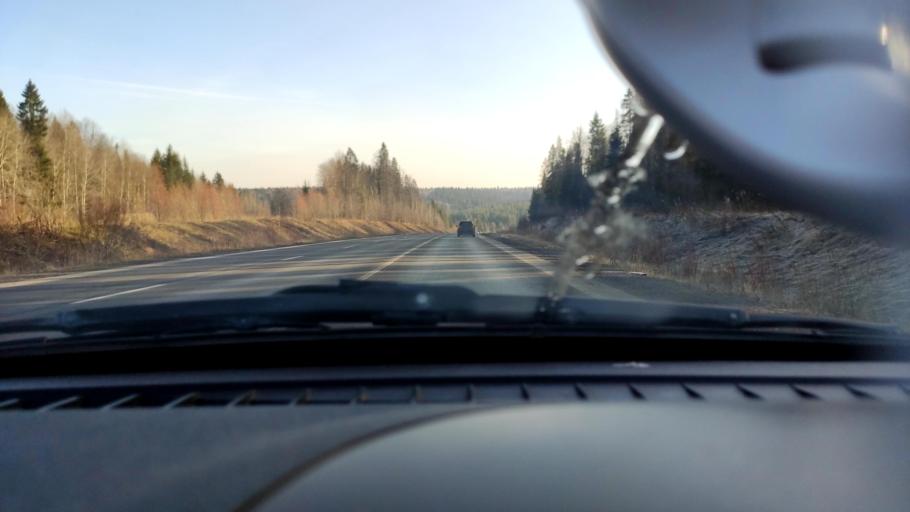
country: RU
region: Perm
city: Novyye Lyady
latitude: 58.0412
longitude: 56.4557
